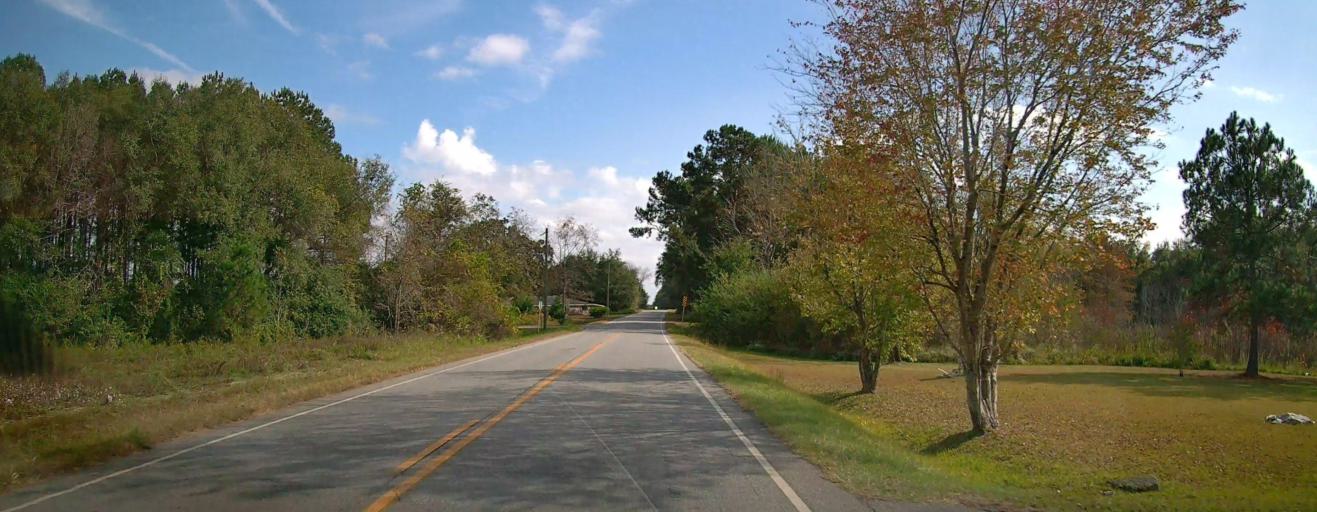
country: US
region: Georgia
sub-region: Thomas County
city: Thomasville
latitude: 30.9337
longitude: -84.0252
